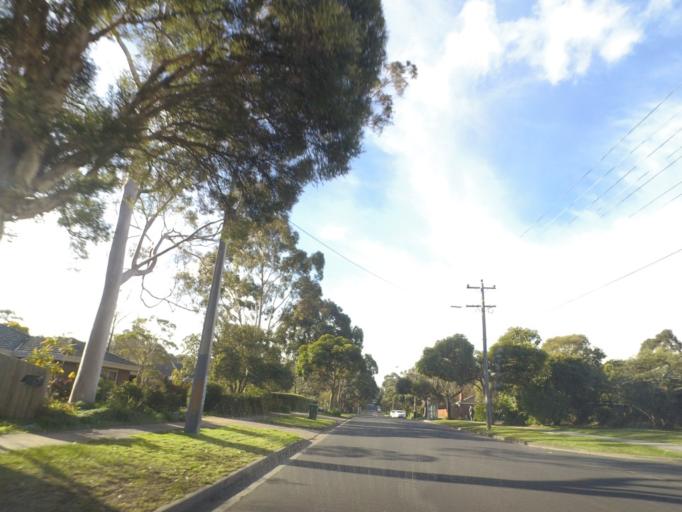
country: AU
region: Victoria
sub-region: Whitehorse
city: Blackburn
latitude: -37.8281
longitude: 145.1489
